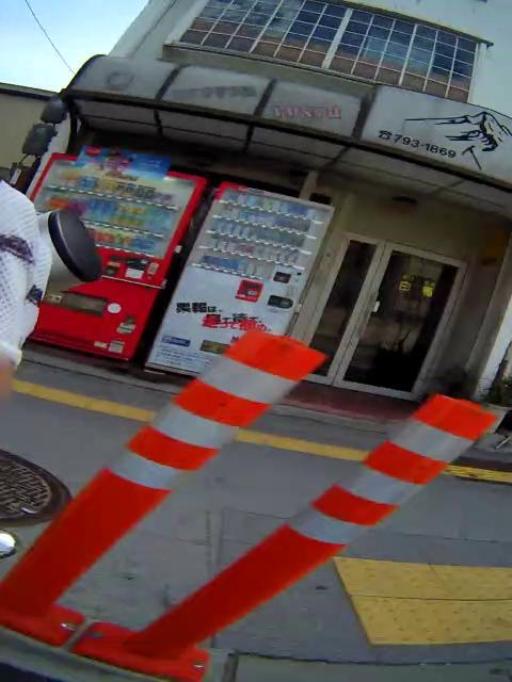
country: JP
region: Osaka
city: Yao
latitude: 34.6262
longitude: 135.5545
